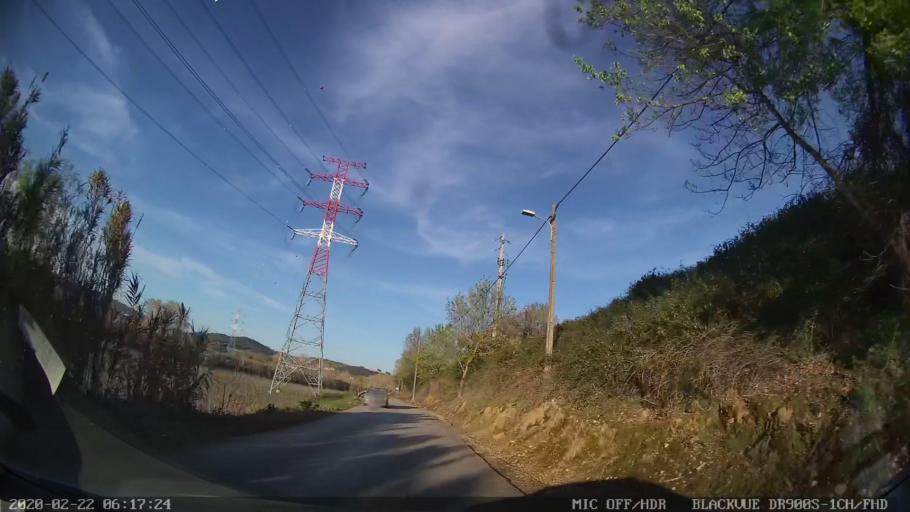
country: PT
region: Lisbon
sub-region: Vila Franca de Xira
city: Castanheira do Ribatejo
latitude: 38.9955
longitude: -9.0111
